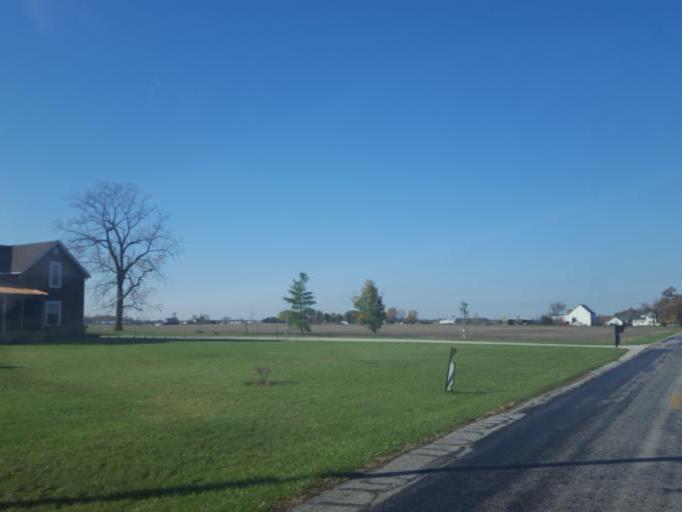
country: US
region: Ohio
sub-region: Marion County
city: Marion
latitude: 40.6010
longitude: -83.0276
